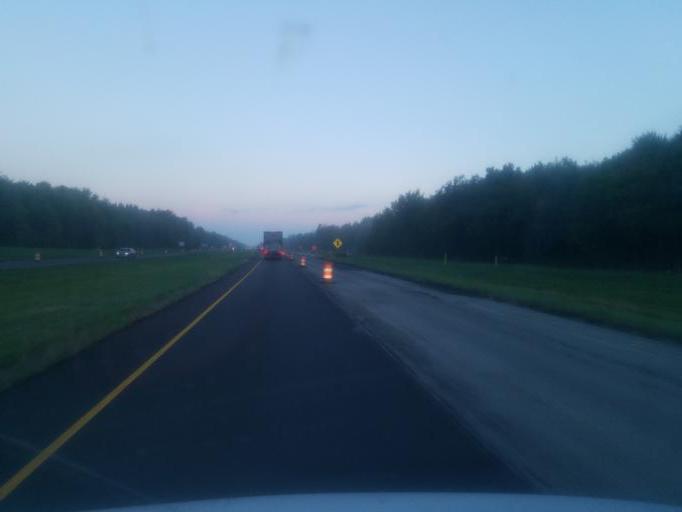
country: US
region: Ohio
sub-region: Ashtabula County
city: Jefferson
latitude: 41.7523
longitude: -80.7120
